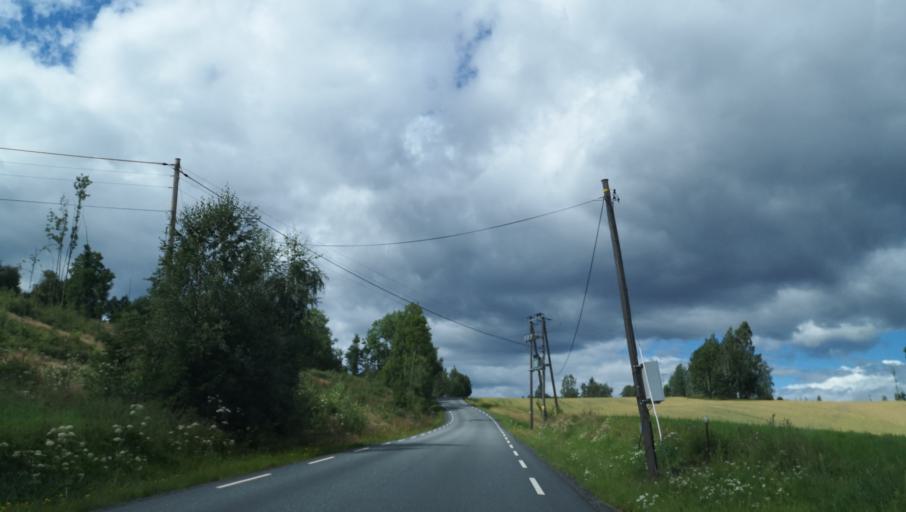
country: NO
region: Ostfold
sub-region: Hobol
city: Tomter
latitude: 59.6715
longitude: 10.9889
